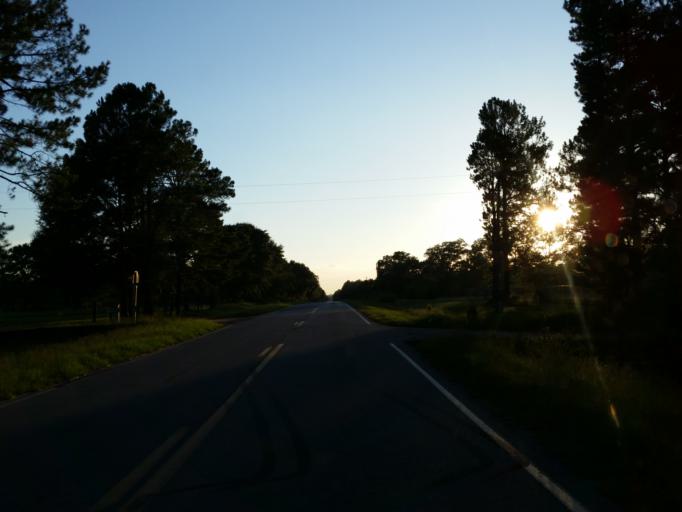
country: US
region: Georgia
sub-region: Berrien County
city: Nashville
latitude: 31.1862
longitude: -83.1627
